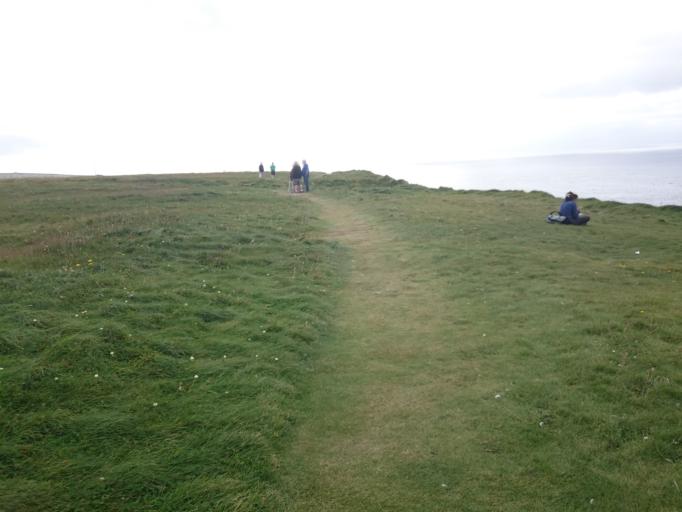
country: IE
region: Munster
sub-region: Ciarrai
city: Ballybunnion
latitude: 52.5618
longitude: -9.9317
